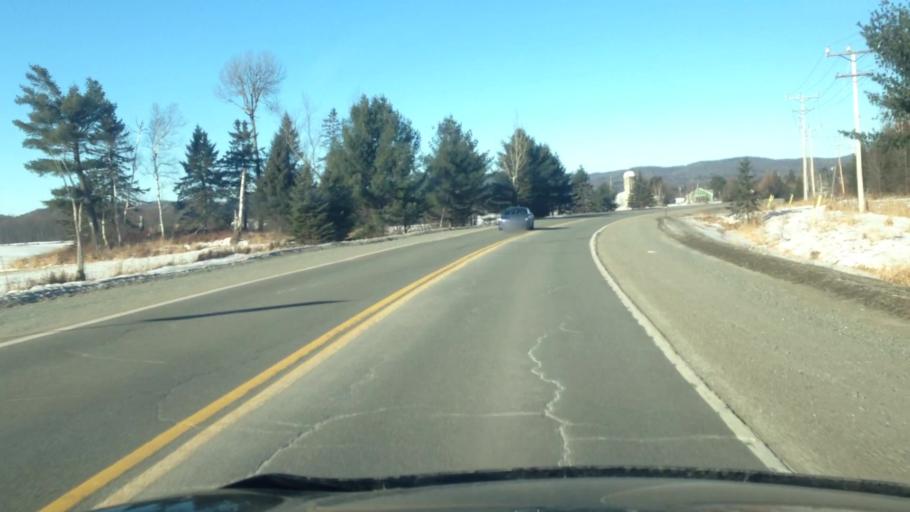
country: CA
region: Quebec
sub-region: Laurentides
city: Mont-Tremblant
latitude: 46.0601
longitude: -74.6216
